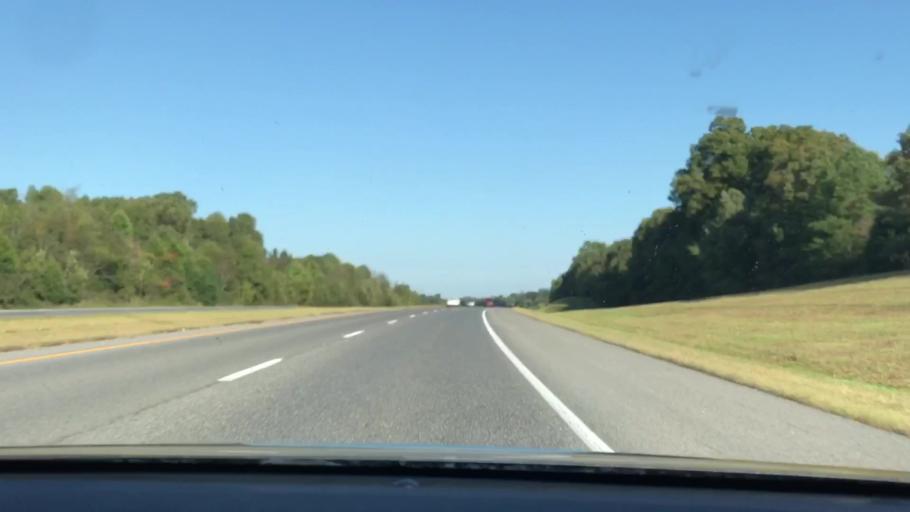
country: US
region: Kentucky
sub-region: Marshall County
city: Benton
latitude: 36.7787
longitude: -88.3218
